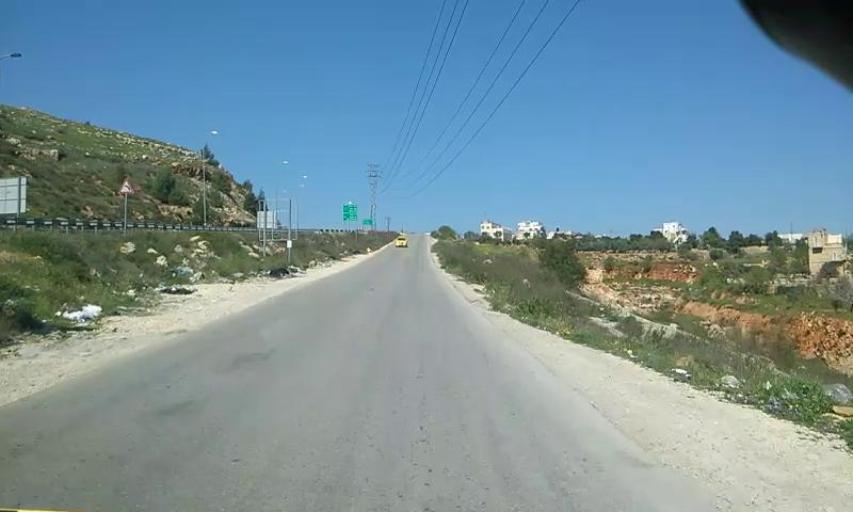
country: PS
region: West Bank
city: Al Khadir
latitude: 31.7061
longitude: 35.1554
